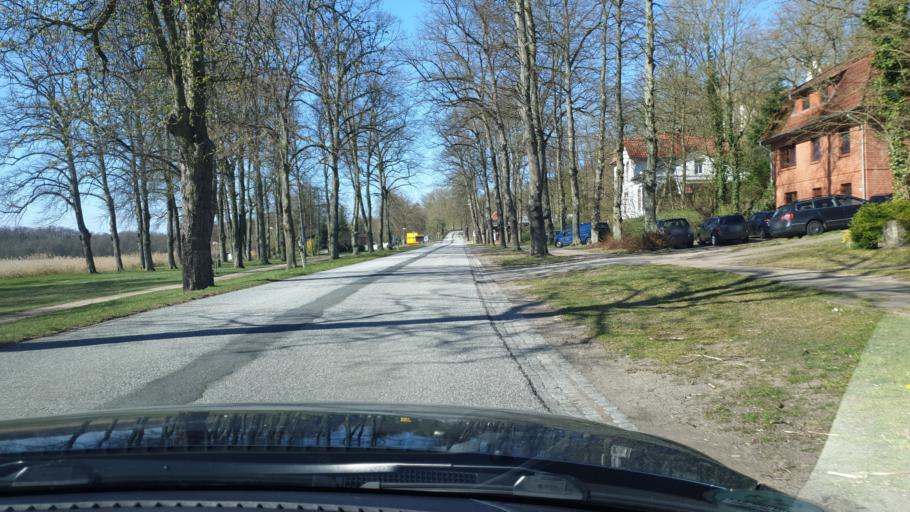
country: DE
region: Mecklenburg-Vorpommern
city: Crivitz
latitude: 53.5802
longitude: 11.6429
